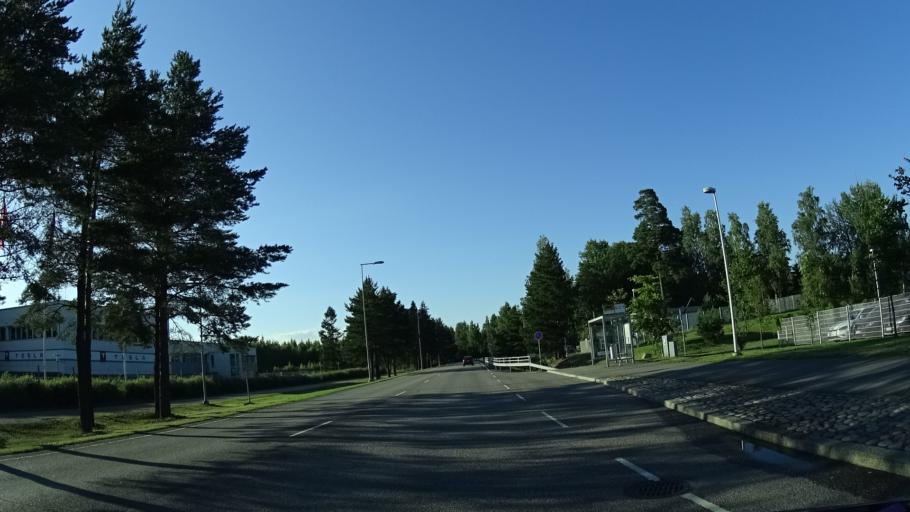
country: FI
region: Uusimaa
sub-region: Helsinki
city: Teekkarikylae
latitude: 60.2698
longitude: 24.8791
